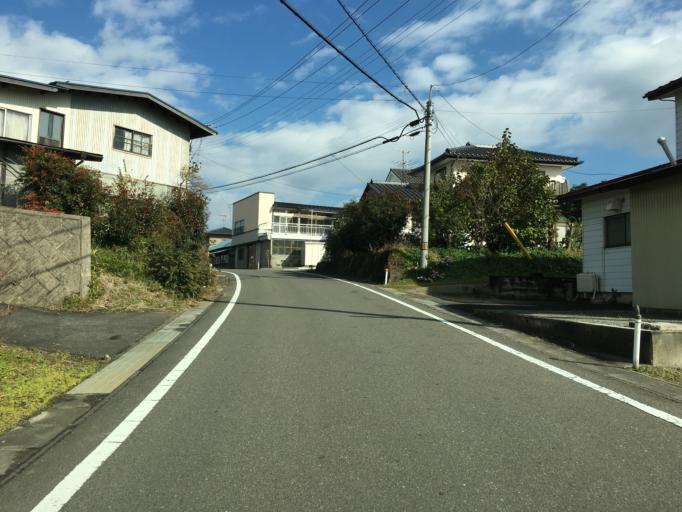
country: JP
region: Fukushima
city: Nihommatsu
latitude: 37.6487
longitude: 140.4827
